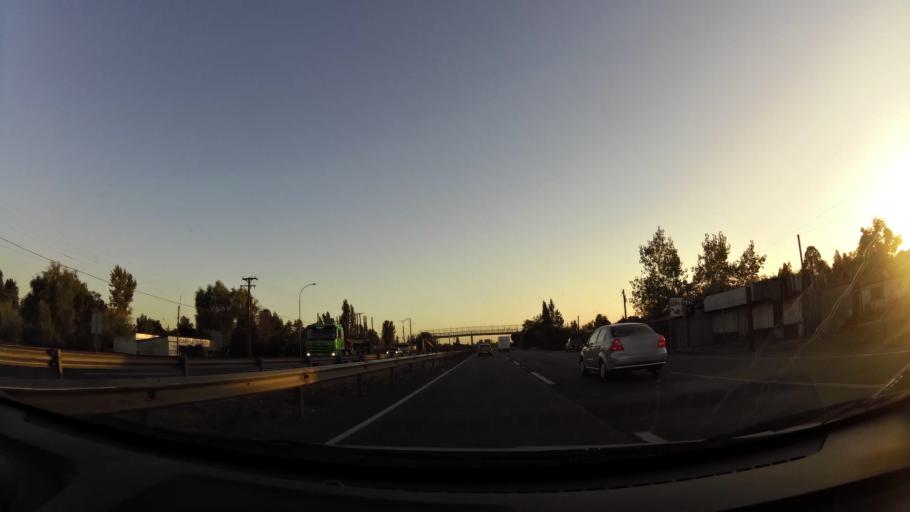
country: CL
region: Maule
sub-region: Provincia de Linares
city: San Javier
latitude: -35.5688
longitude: -71.6982
